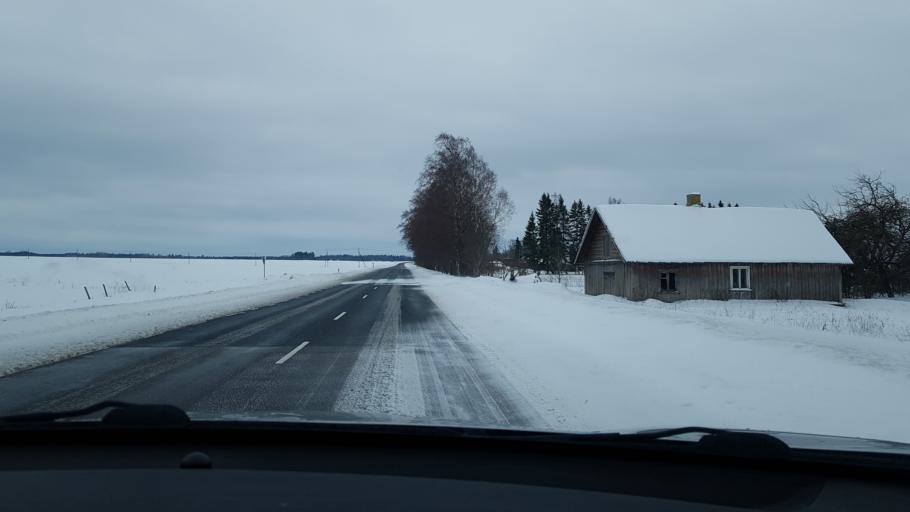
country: EE
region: Jaervamaa
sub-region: Jaerva-Jaani vald
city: Jarva-Jaani
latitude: 59.1231
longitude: 25.7865
